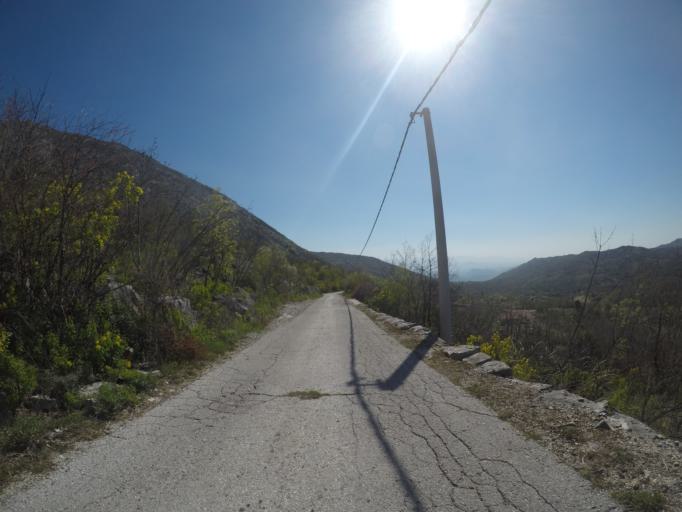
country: ME
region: Danilovgrad
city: Danilovgrad
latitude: 42.5293
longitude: 19.0303
